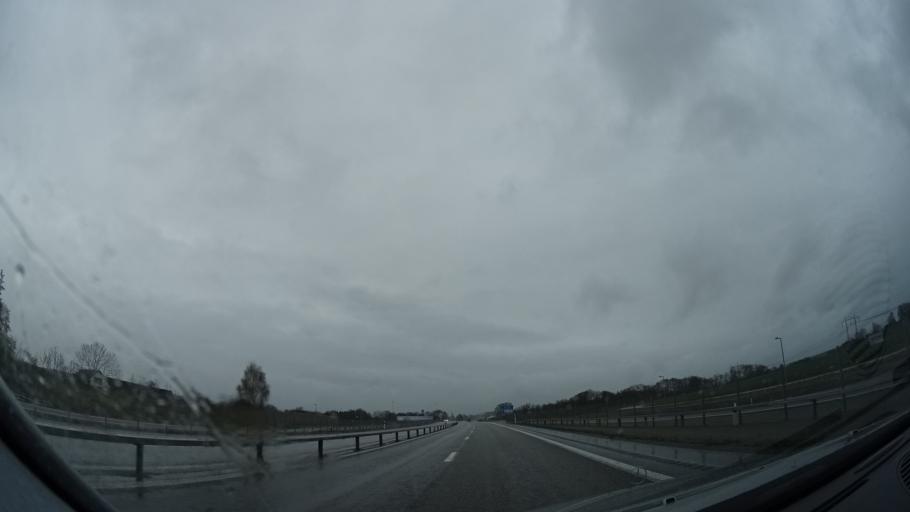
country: SE
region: Skane
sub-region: Hoors Kommun
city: Loberod
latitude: 55.8055
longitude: 13.4644
